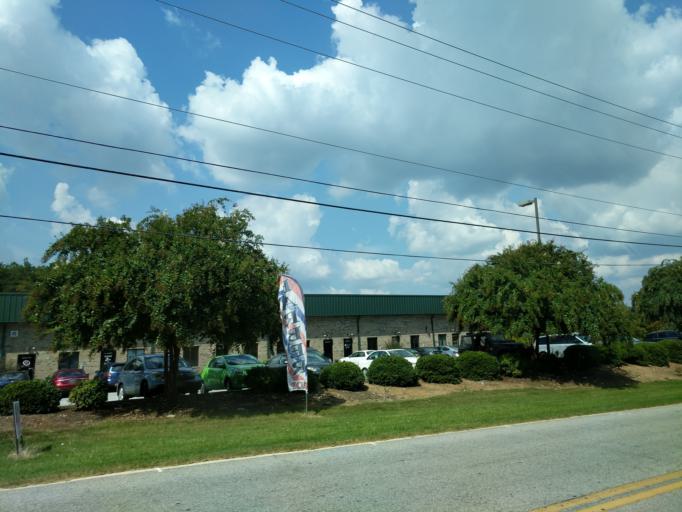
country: US
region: South Carolina
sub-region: Greenville County
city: Mauldin
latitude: 34.8345
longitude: -82.2900
